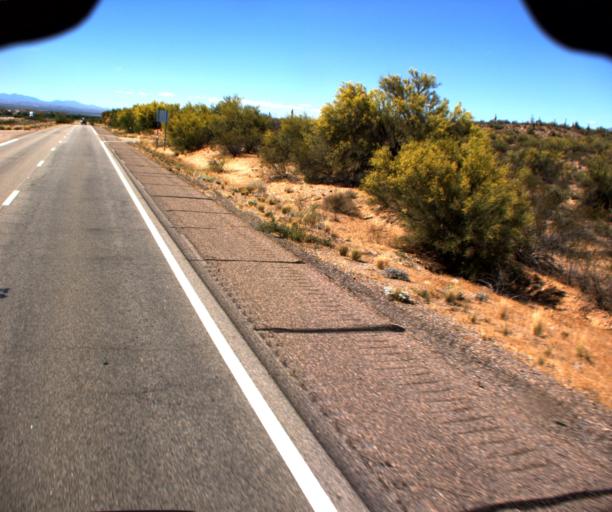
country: US
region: Arizona
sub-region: Yavapai County
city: Bagdad
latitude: 34.6527
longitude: -113.5732
